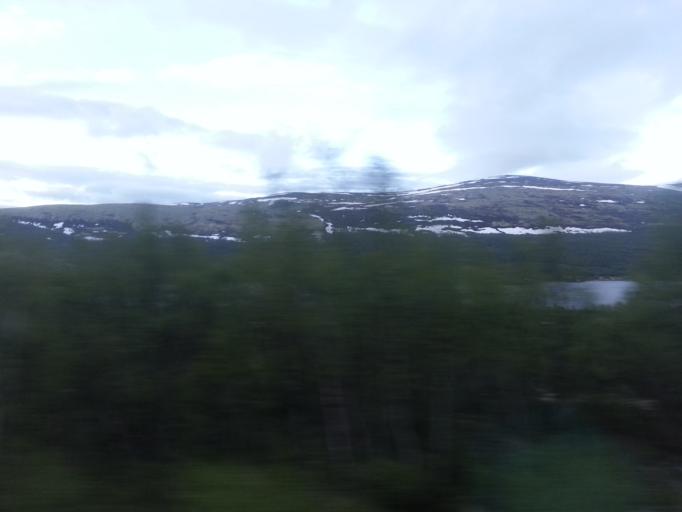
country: NO
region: Oppland
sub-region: Dovre
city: Dovre
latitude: 62.1799
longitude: 9.4645
